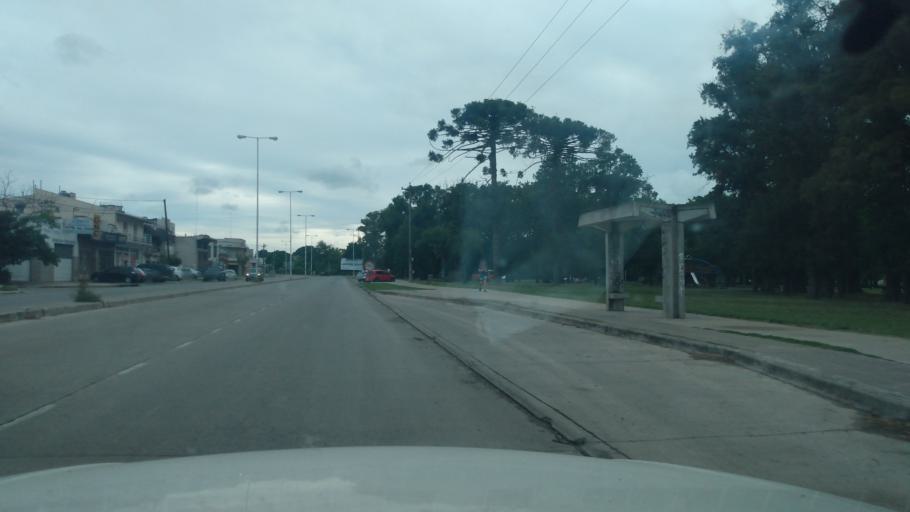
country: AR
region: Buenos Aires
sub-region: Partido de Lujan
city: Lujan
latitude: -34.5582
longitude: -59.1139
